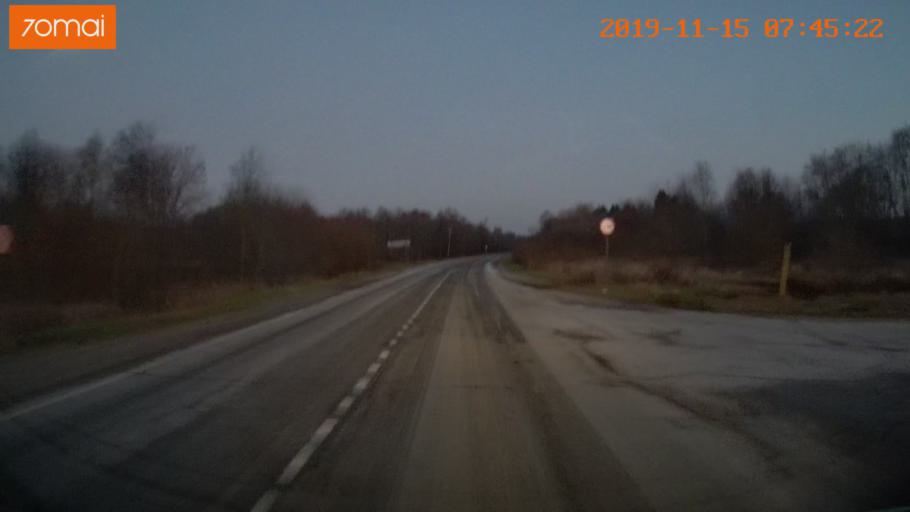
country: RU
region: Vologda
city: Sheksna
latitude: 58.8234
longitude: 38.2981
